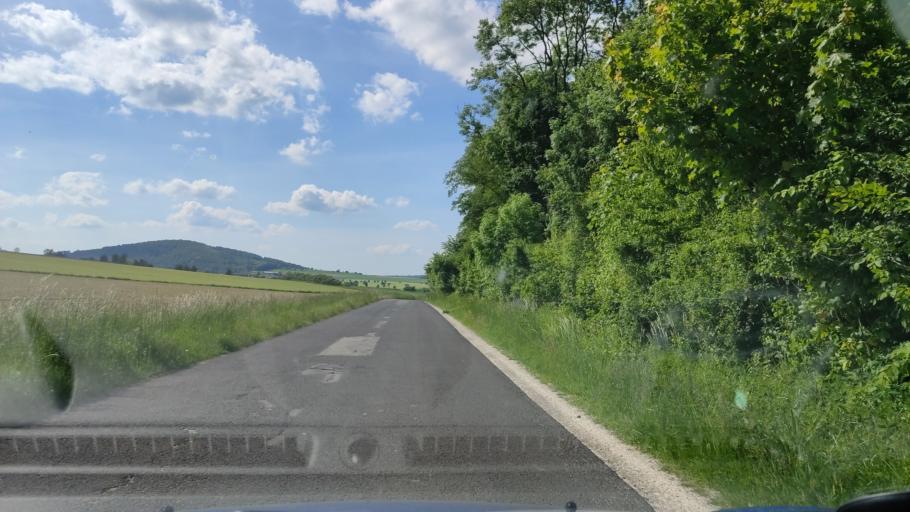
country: DE
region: Lower Saxony
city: Adelebsen
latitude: 51.5479
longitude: 9.8010
